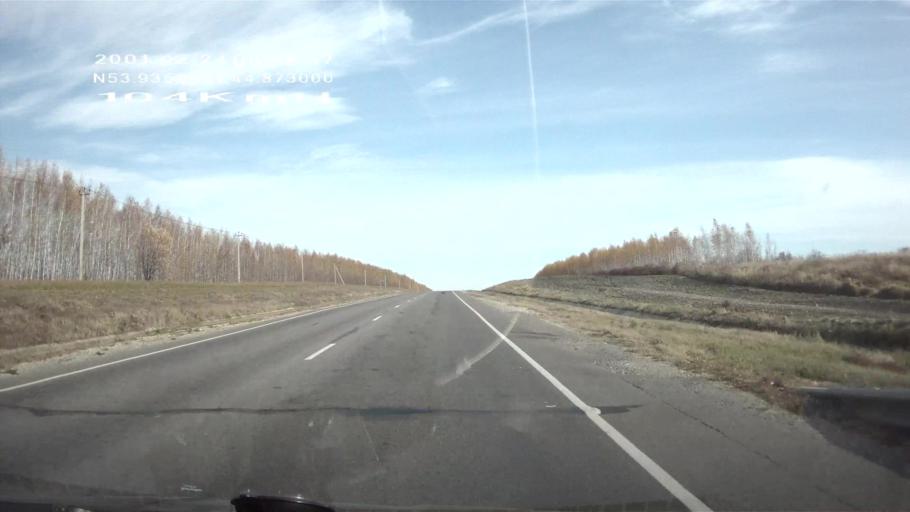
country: RU
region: Penza
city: Issa
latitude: 53.9363
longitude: 44.8734
